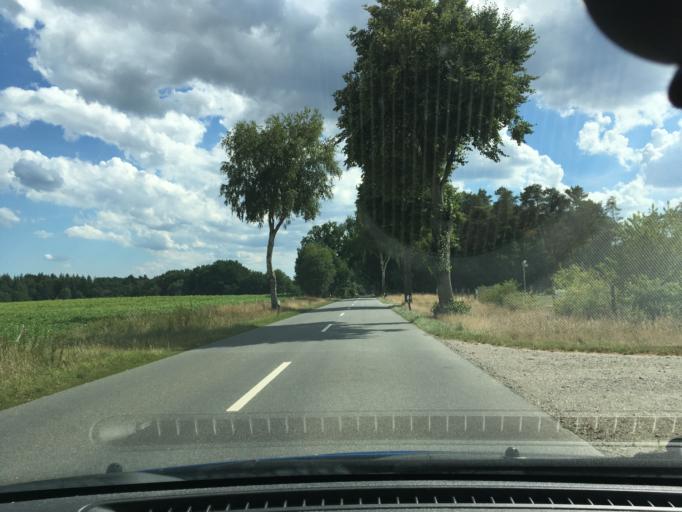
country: DE
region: Lower Saxony
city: Rehlingen
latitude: 53.0677
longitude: 10.2335
